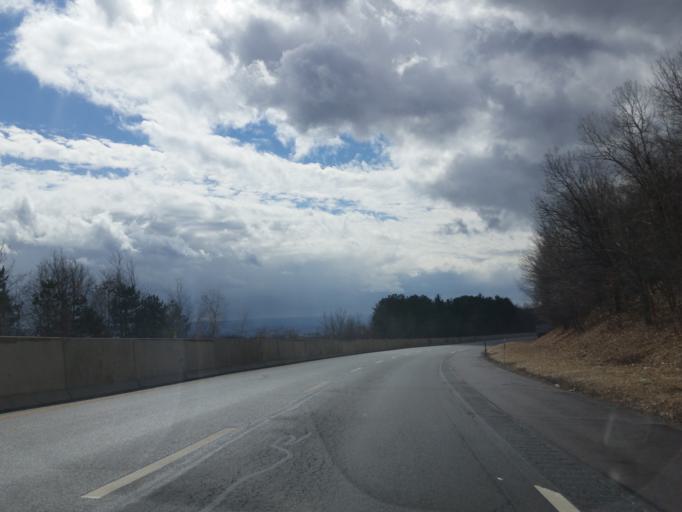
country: US
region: Pennsylvania
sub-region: Lackawanna County
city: Taylor
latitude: 41.4084
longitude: -75.7218
